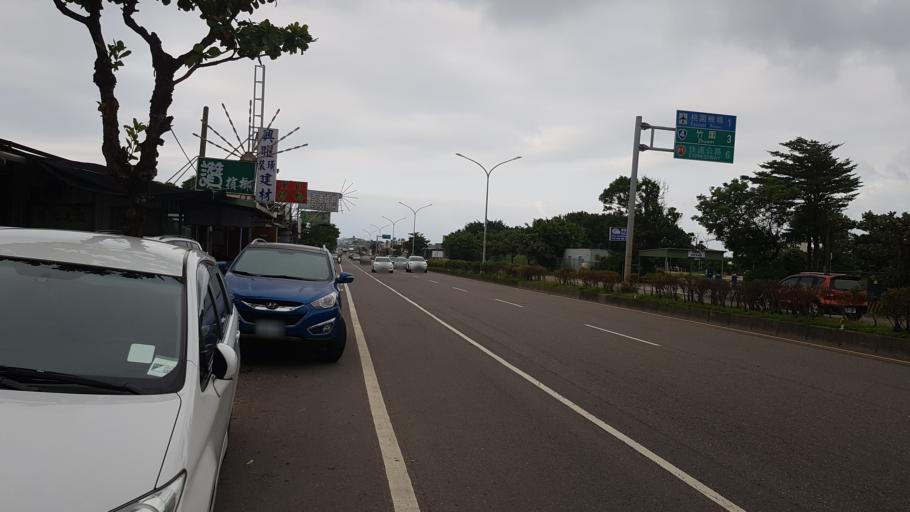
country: TW
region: Taiwan
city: Taoyuan City
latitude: 25.0796
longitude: 121.2585
